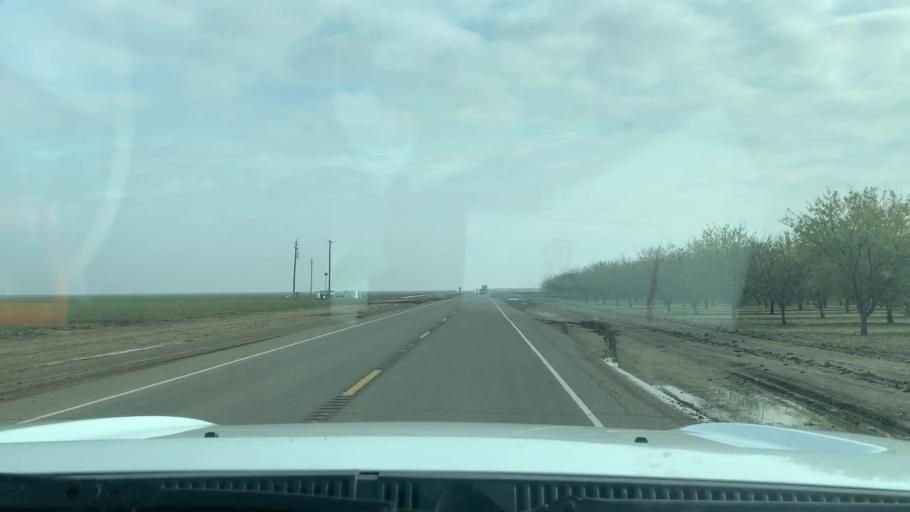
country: US
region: California
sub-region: Fresno County
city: Huron
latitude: 36.2554
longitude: -120.0323
